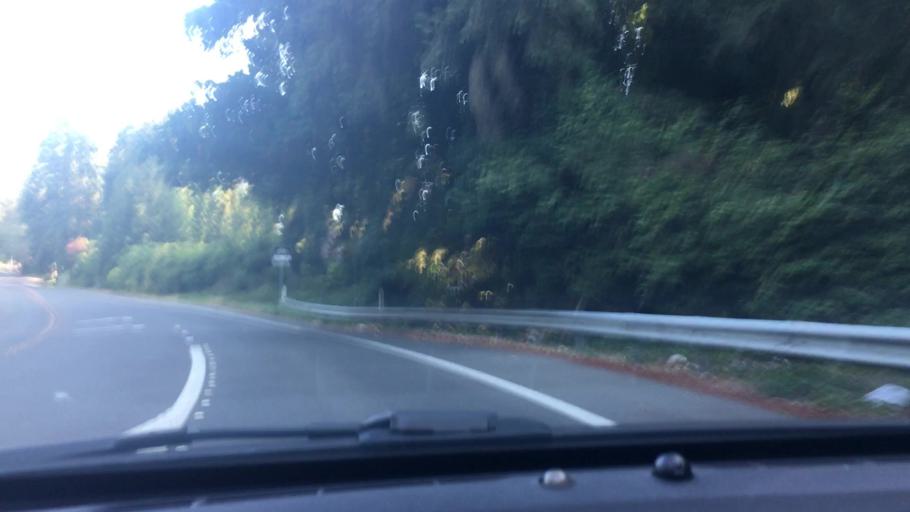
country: US
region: Washington
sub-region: King County
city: Sammamish
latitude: 47.6169
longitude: -122.1072
